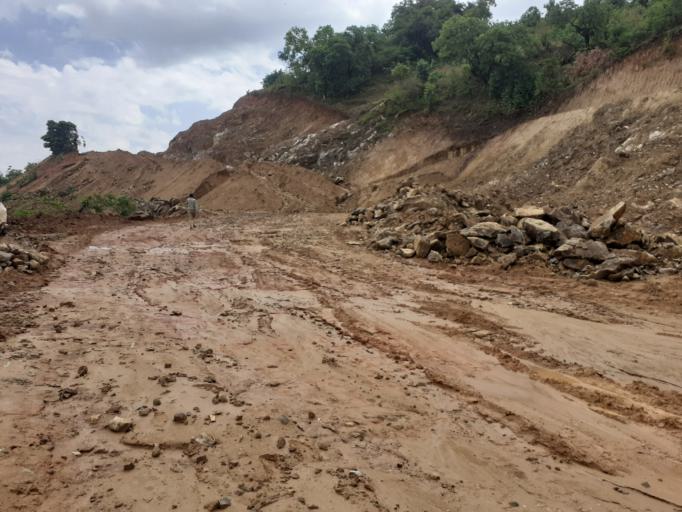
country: ET
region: Oromiya
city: Gimbi
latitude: 9.3261
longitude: 35.6922
